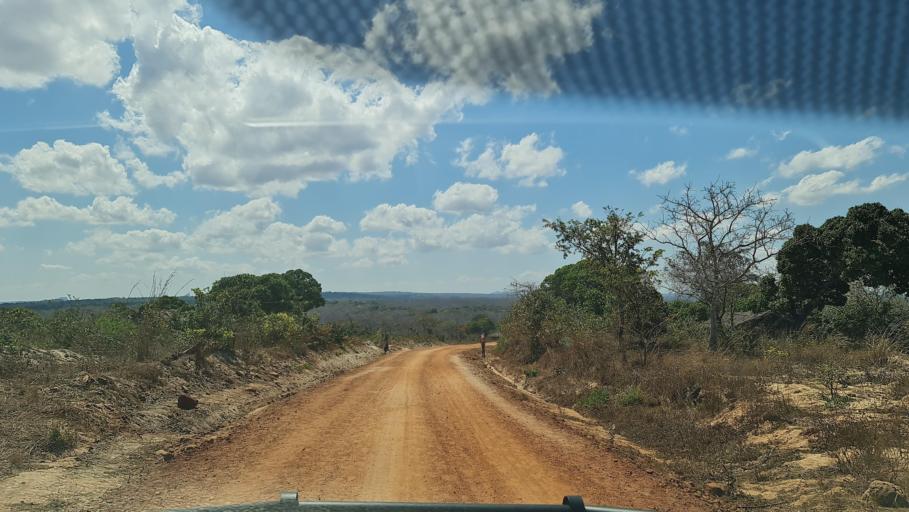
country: MZ
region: Nampula
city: Nacala
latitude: -14.1756
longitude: 40.2149
